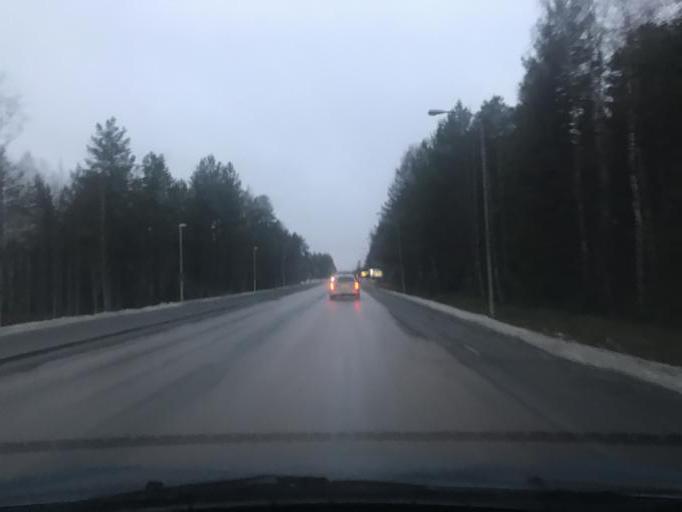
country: SE
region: Norrbotten
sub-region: Lulea Kommun
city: Gammelstad
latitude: 65.6277
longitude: 22.0370
